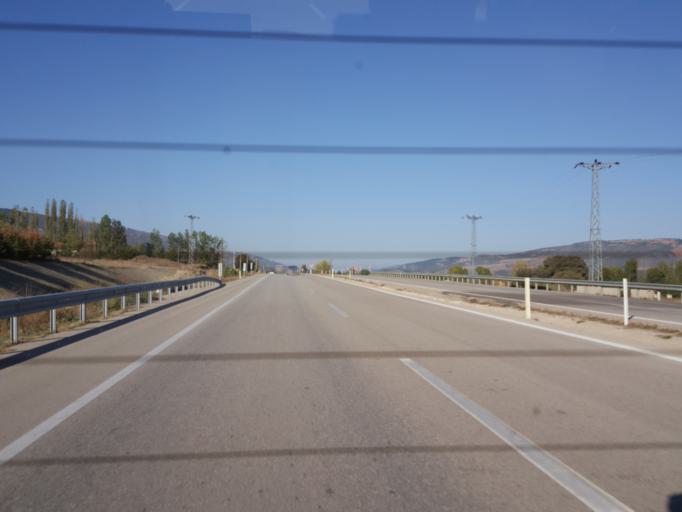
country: TR
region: Amasya
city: Ezinepazari
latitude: 40.5690
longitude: 36.0800
